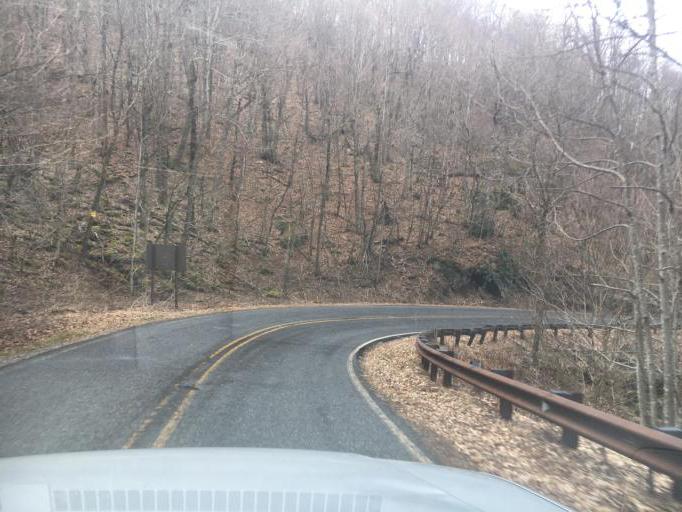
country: US
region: North Carolina
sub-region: Transylvania County
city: Brevard
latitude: 35.3673
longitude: -82.7951
